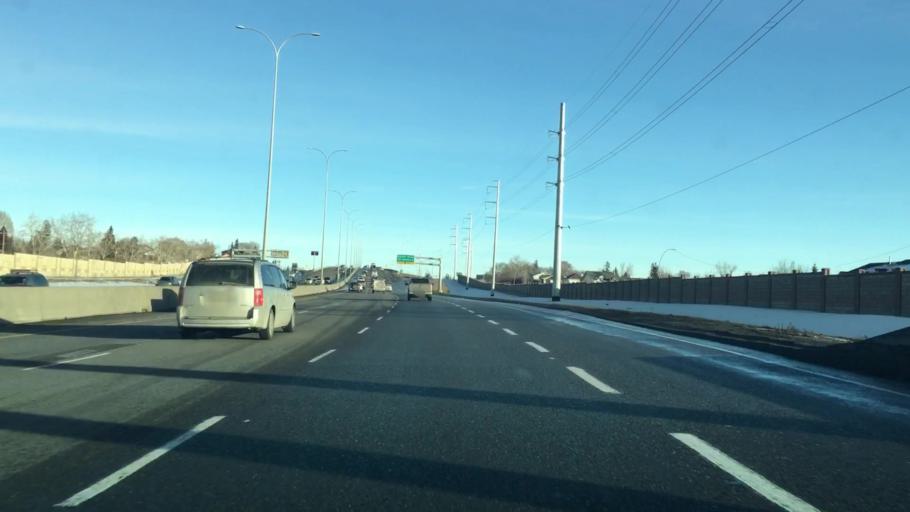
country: CA
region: Alberta
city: Calgary
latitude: 50.9792
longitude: -114.0082
